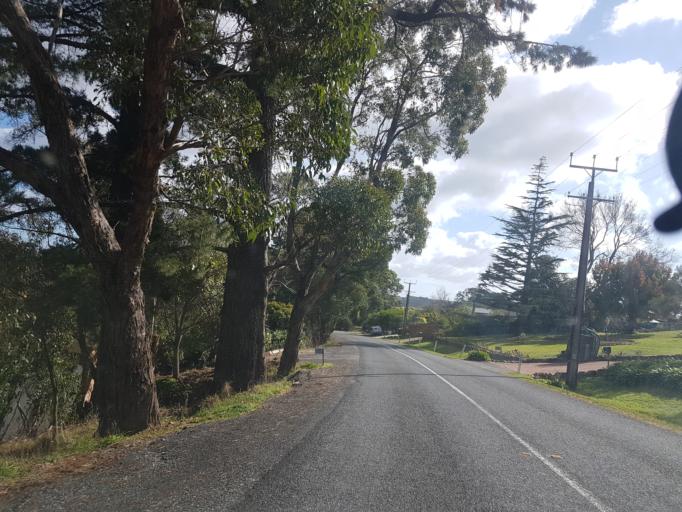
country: AU
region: South Australia
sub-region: Adelaide Hills
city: Upper Sturt
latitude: -35.0455
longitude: 138.6918
